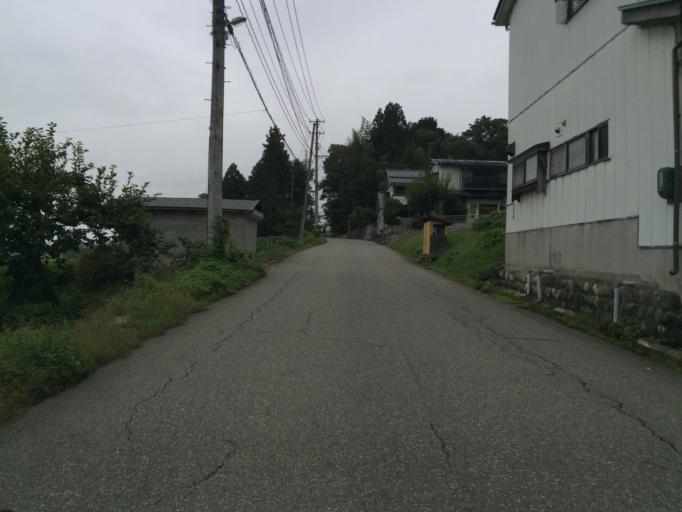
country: JP
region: Fukushima
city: Kitakata
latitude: 37.5085
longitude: 139.9551
